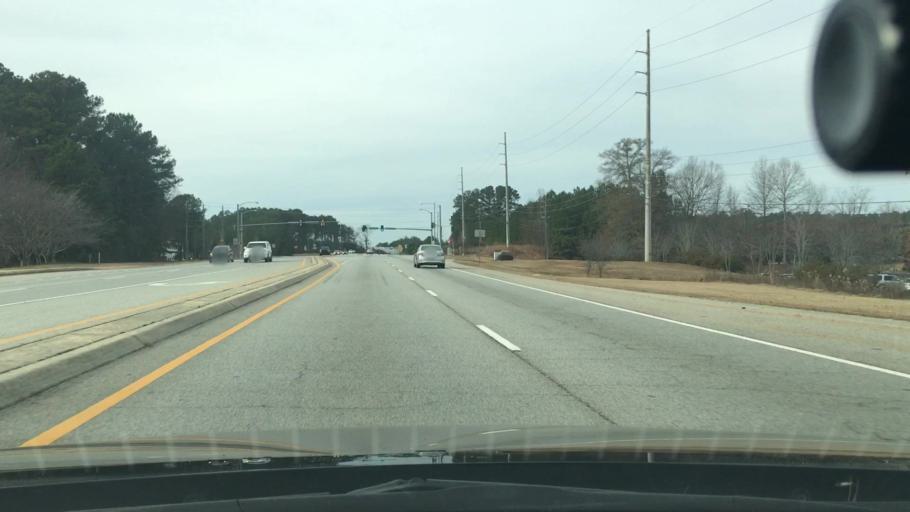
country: US
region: Georgia
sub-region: Coweta County
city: Senoia
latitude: 33.3525
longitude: -84.5548
